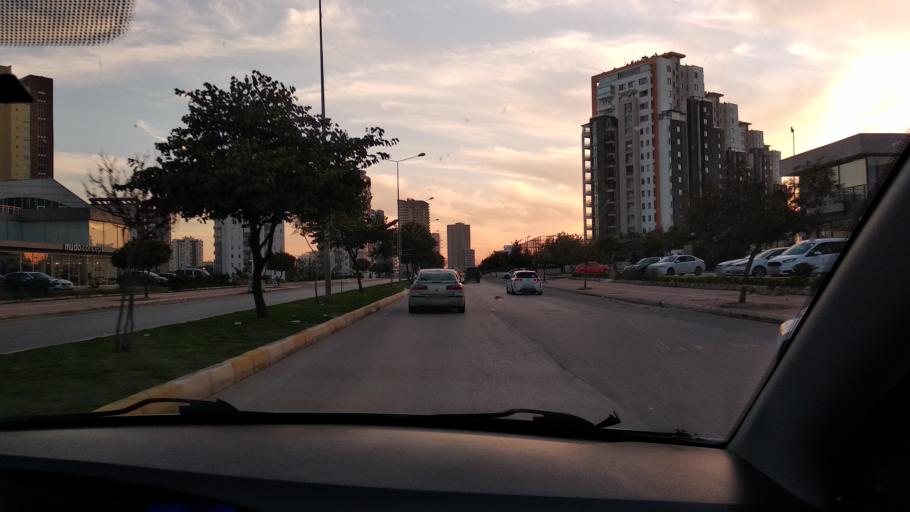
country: TR
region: Mersin
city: Mercin
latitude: 36.8061
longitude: 34.5872
